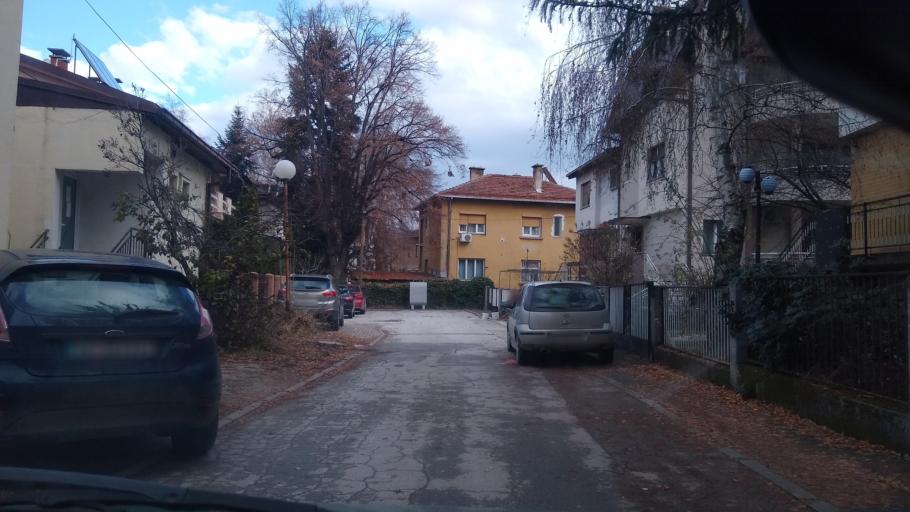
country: MK
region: Bitola
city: Bitola
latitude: 41.0240
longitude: 21.3336
